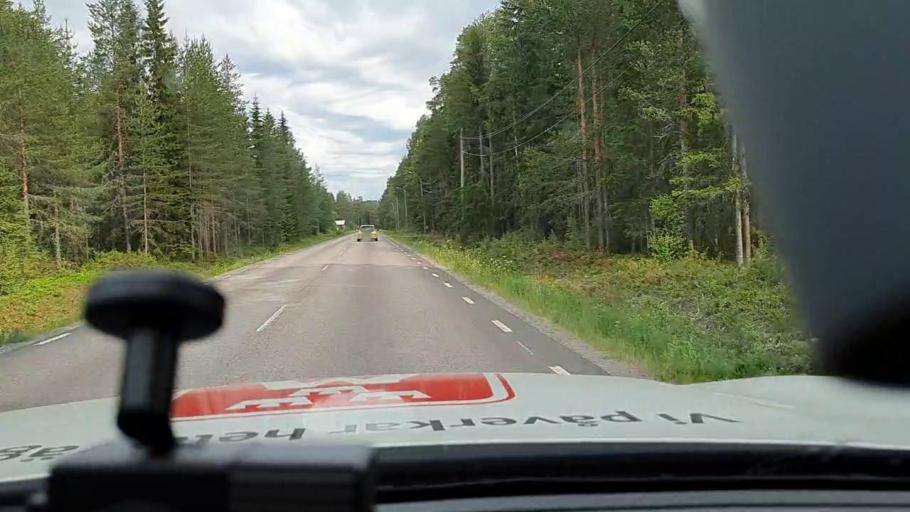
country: SE
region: Norrbotten
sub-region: Bodens Kommun
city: Saevast
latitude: 65.7271
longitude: 21.7454
